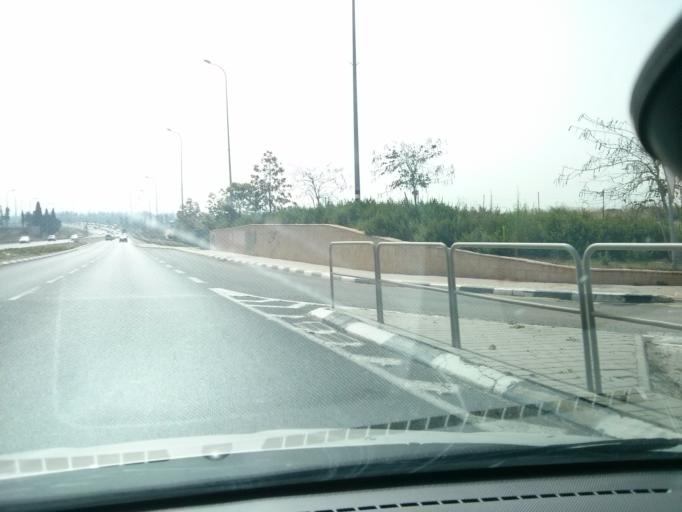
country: IL
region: Central District
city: Even Yehuda
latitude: 32.2552
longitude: 34.8797
